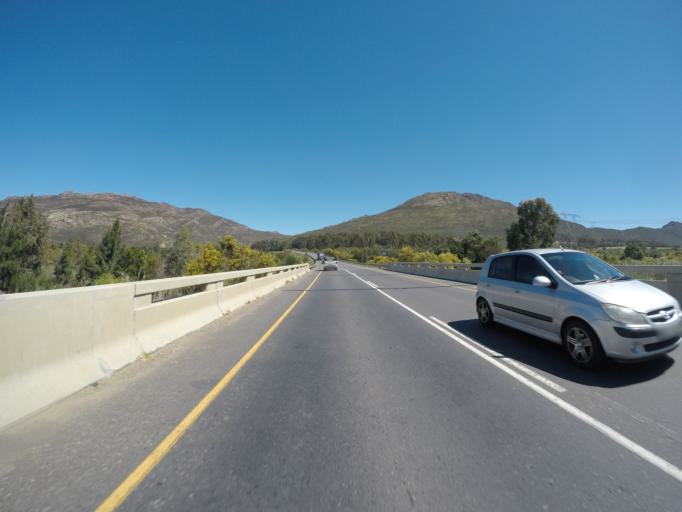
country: ZA
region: Western Cape
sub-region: Cape Winelands District Municipality
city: Ceres
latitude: -33.3105
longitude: 19.1005
